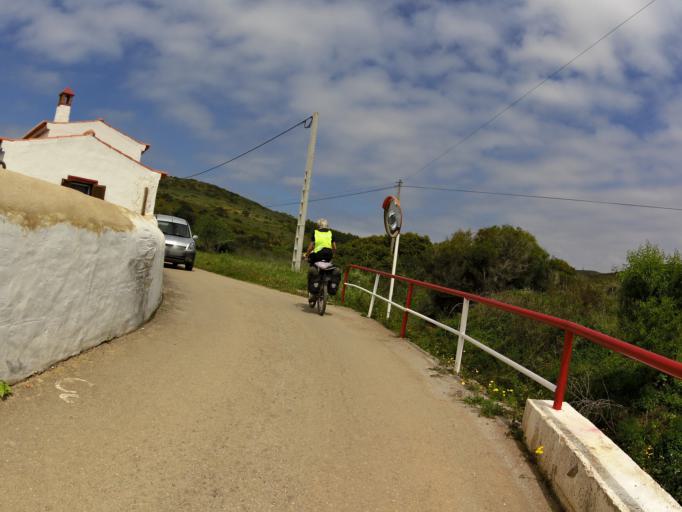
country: PT
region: Faro
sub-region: Vila do Bispo
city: Vila do Bispo
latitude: 37.0673
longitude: -8.8577
